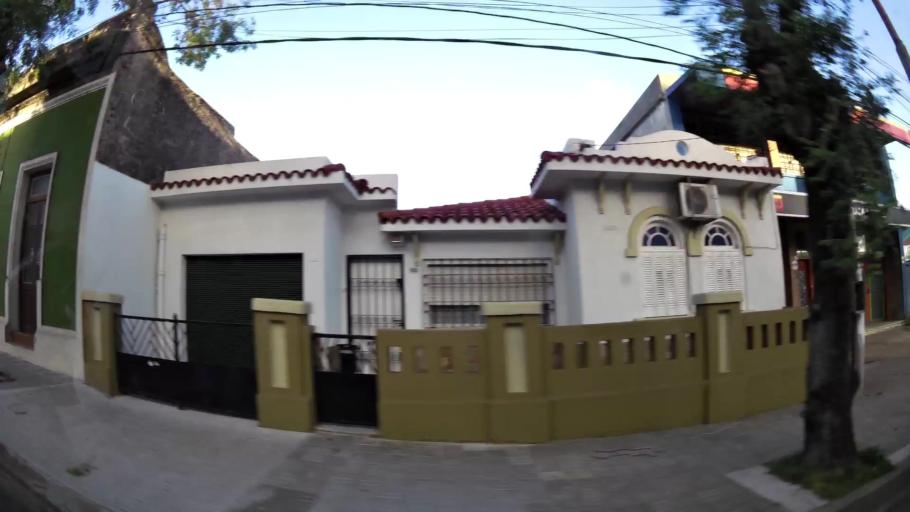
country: UY
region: Montevideo
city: Montevideo
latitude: -34.8789
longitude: -56.2503
